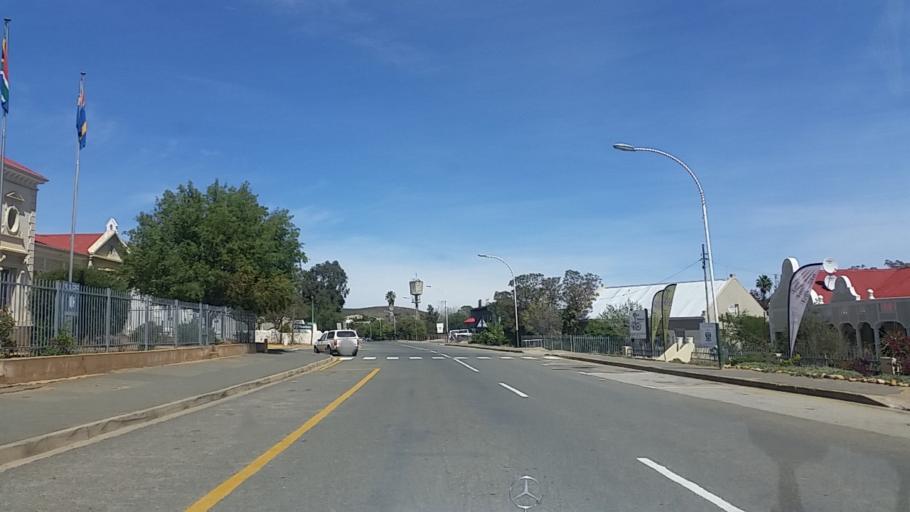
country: ZA
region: Western Cape
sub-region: Eden District Municipality
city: Knysna
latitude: -33.6569
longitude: 23.1259
